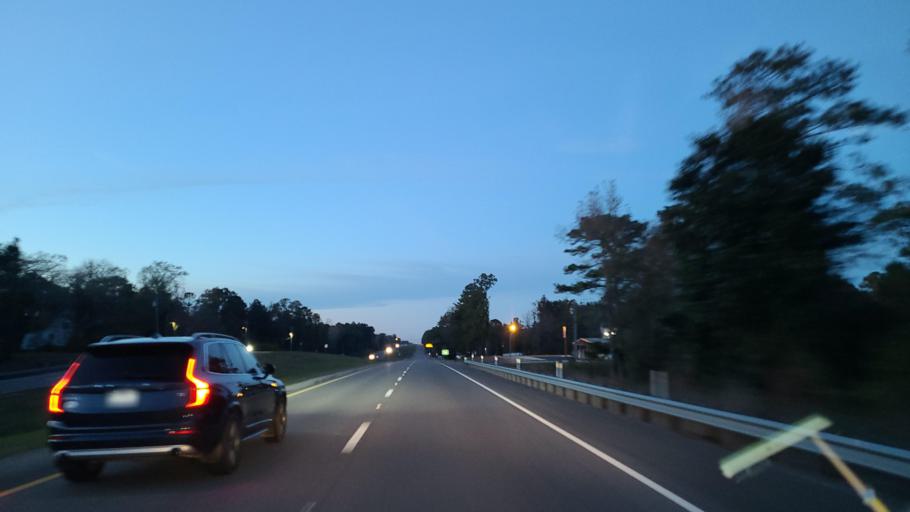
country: US
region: Mississippi
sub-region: Forrest County
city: Hattiesburg
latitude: 31.2093
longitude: -89.2608
